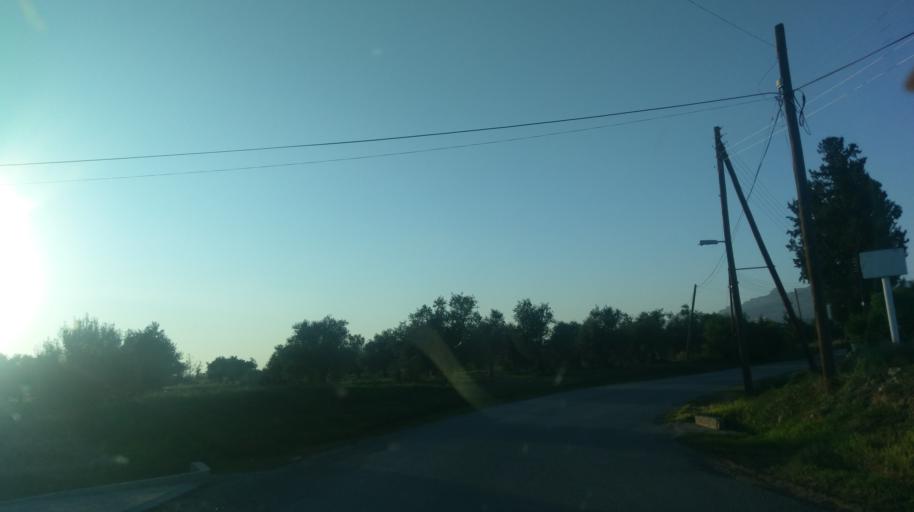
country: CY
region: Lefkosia
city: Nicosia
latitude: 35.2372
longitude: 33.4995
